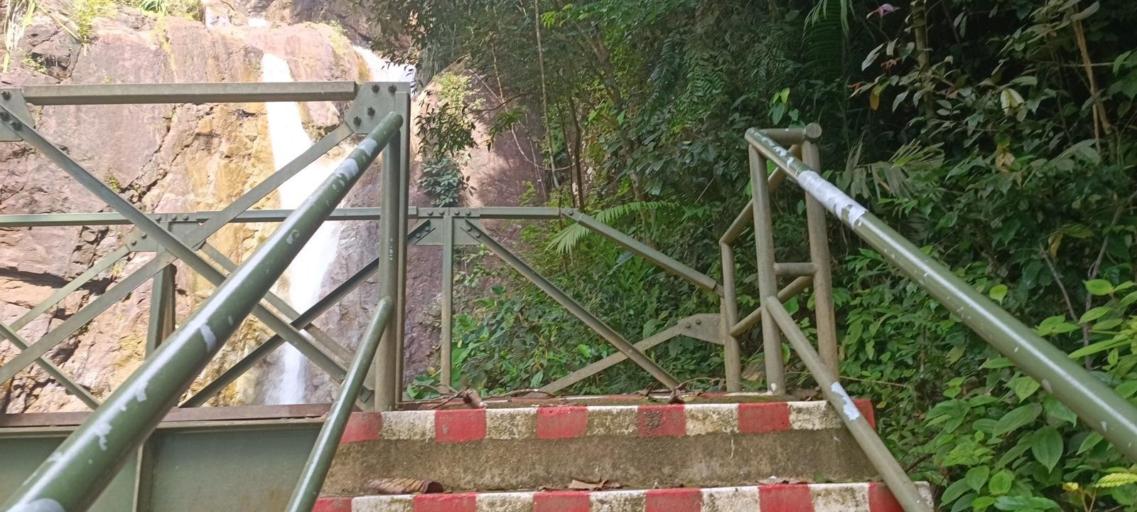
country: MY
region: Penang
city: Tanjung Tokong
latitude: 5.4406
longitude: 100.2829
